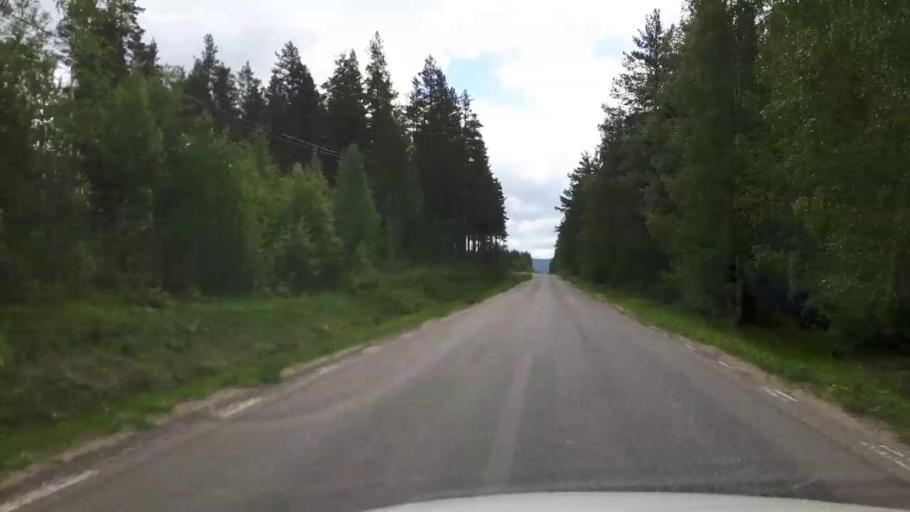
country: SE
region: Gaevleborg
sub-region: Ovanakers Kommun
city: Alfta
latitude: 61.3263
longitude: 15.9724
